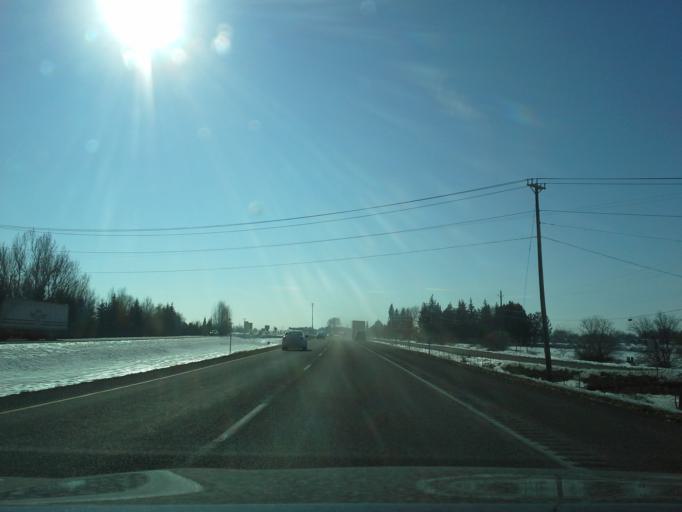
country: US
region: Idaho
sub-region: Bonneville County
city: Idaho Falls
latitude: 43.4866
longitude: -112.0599
